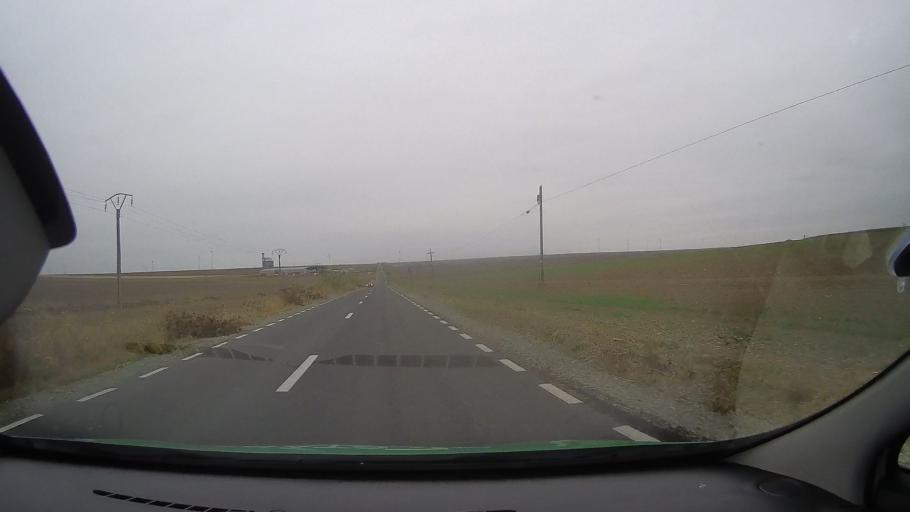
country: RO
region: Constanta
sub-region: Comuna Tortoman
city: Tortoman
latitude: 44.3589
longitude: 28.2109
